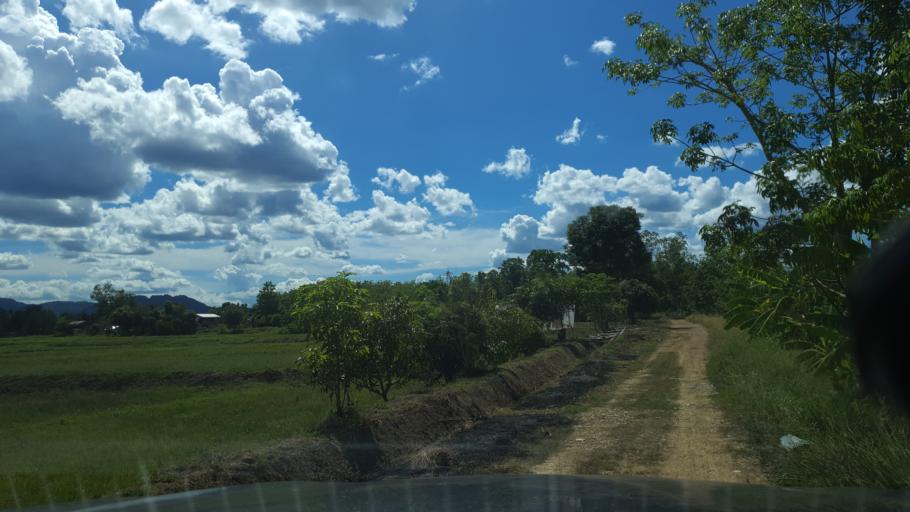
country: TH
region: Sukhothai
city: Thung Saliam
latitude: 17.3394
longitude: 99.4395
